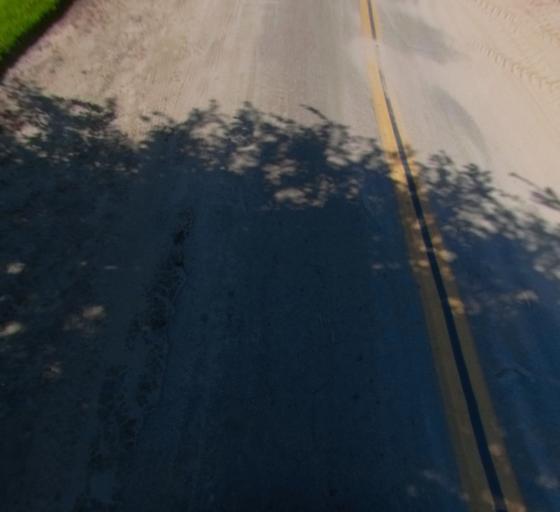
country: US
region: California
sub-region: Fresno County
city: Biola
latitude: 36.8226
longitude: -120.0247
